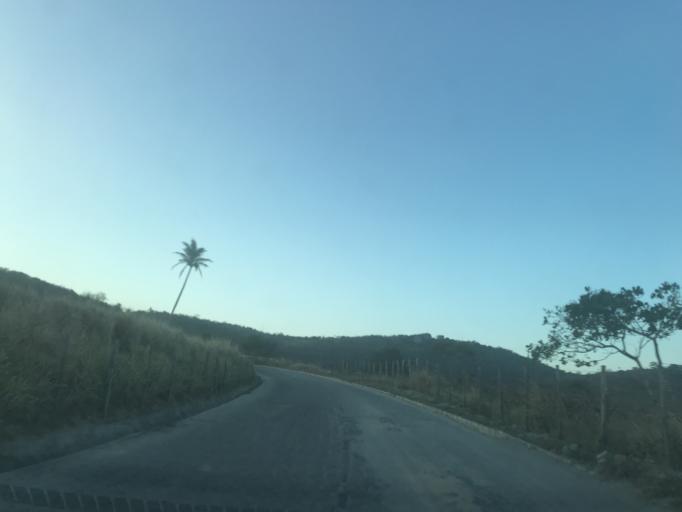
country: BR
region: Pernambuco
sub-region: Bezerros
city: Bezerros
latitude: -8.1935
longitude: -35.7571
